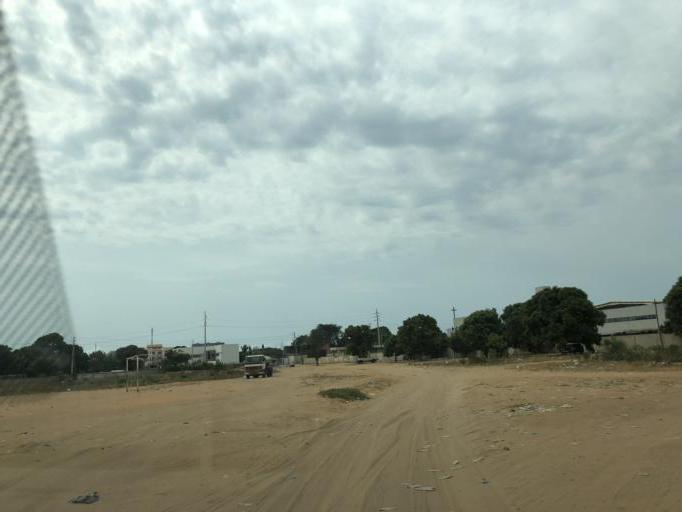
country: AO
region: Luanda
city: Luanda
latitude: -8.8905
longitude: 13.1911
